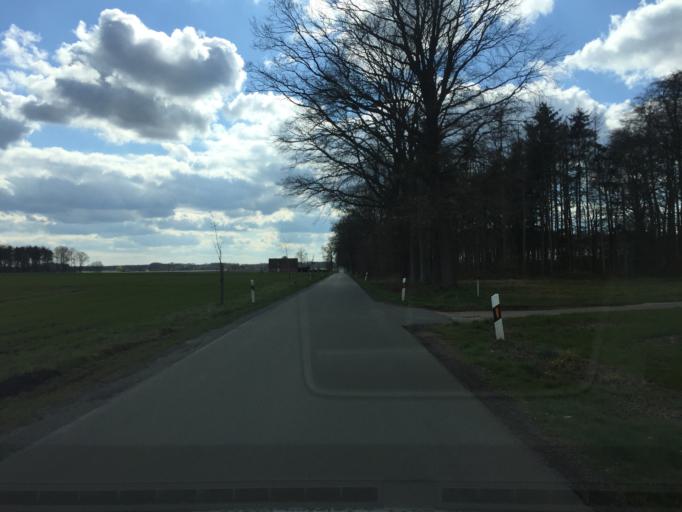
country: DE
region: Lower Saxony
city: Engeln
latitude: 52.7758
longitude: 8.9405
